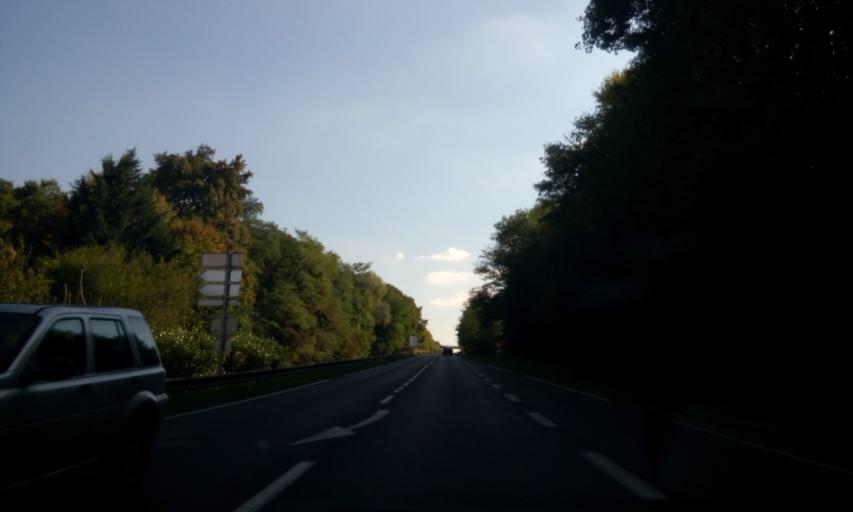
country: FR
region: Centre
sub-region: Departement d'Indre-et-Loire
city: Charge
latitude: 47.4233
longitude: 1.0129
